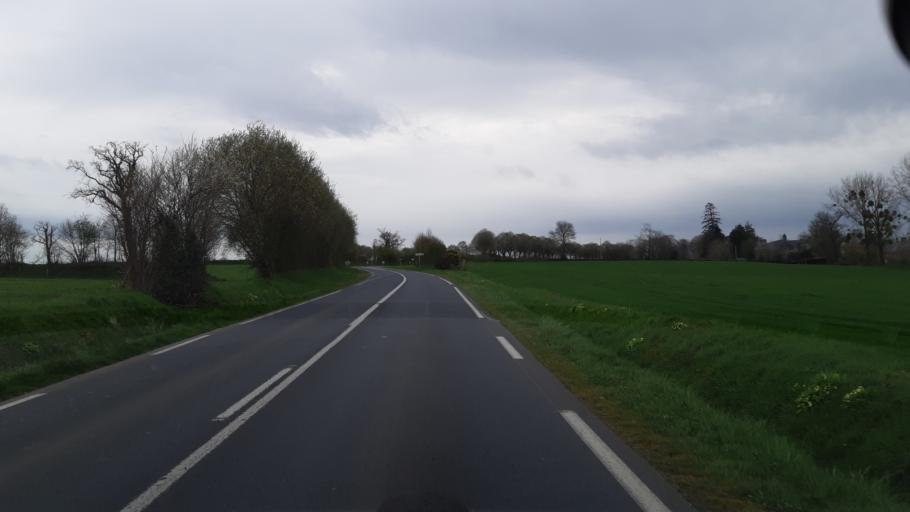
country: FR
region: Lower Normandy
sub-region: Departement de la Manche
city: Agneaux
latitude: 49.0343
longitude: -1.1346
